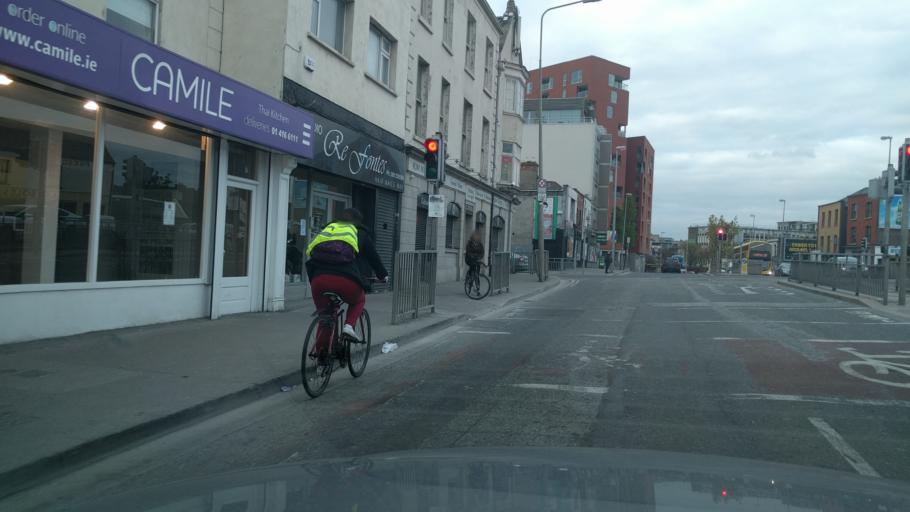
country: IE
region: Leinster
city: Rialto
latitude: 53.3333
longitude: -6.2917
